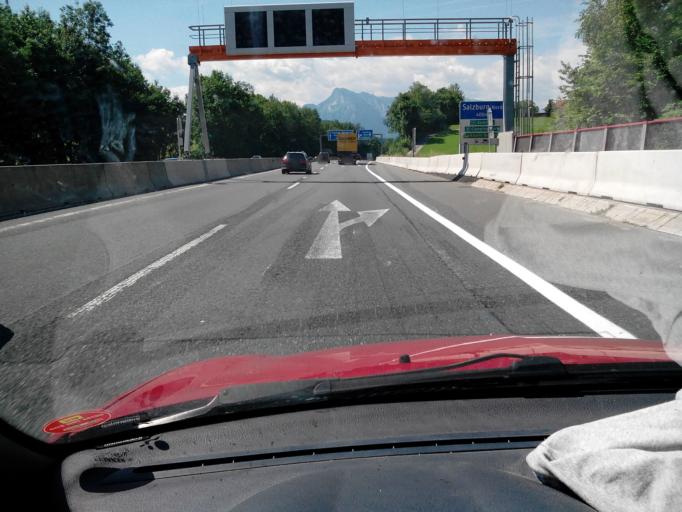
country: AT
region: Salzburg
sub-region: Politischer Bezirk Salzburg-Umgebung
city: Hallwang
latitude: 47.8347
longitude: 13.0728
